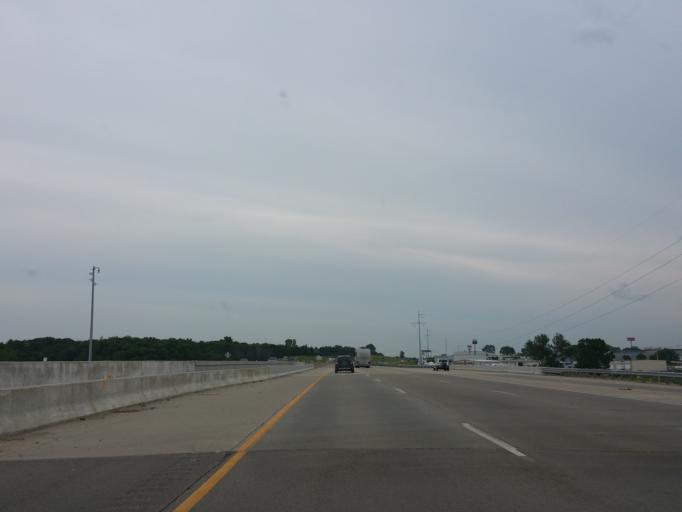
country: US
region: Wisconsin
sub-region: Dane County
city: Windsor
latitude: 43.1796
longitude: -89.3253
